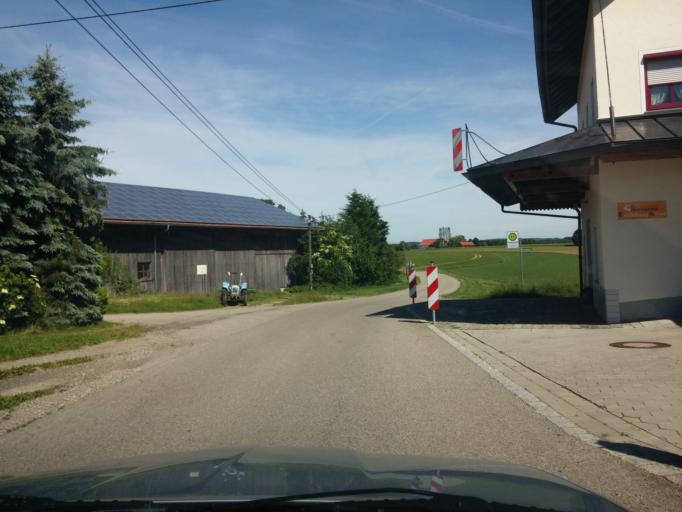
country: DE
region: Bavaria
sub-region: Swabia
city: Woringen
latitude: 47.8930
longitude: 10.1852
